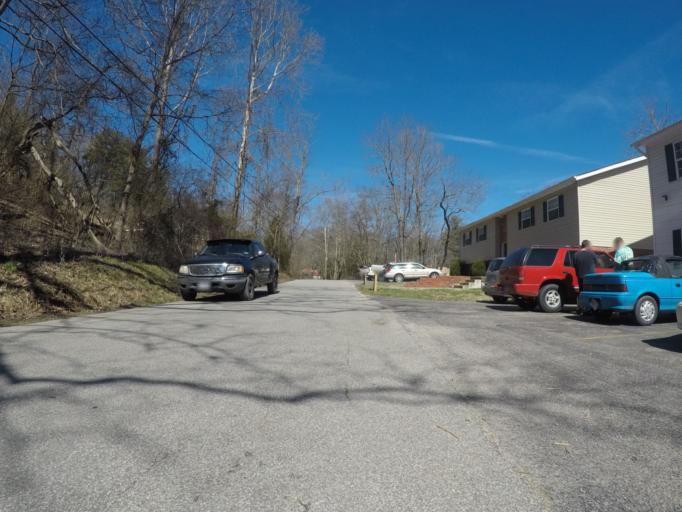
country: US
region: Ohio
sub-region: Lawrence County
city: Burlington
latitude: 38.4542
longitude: -82.5026
